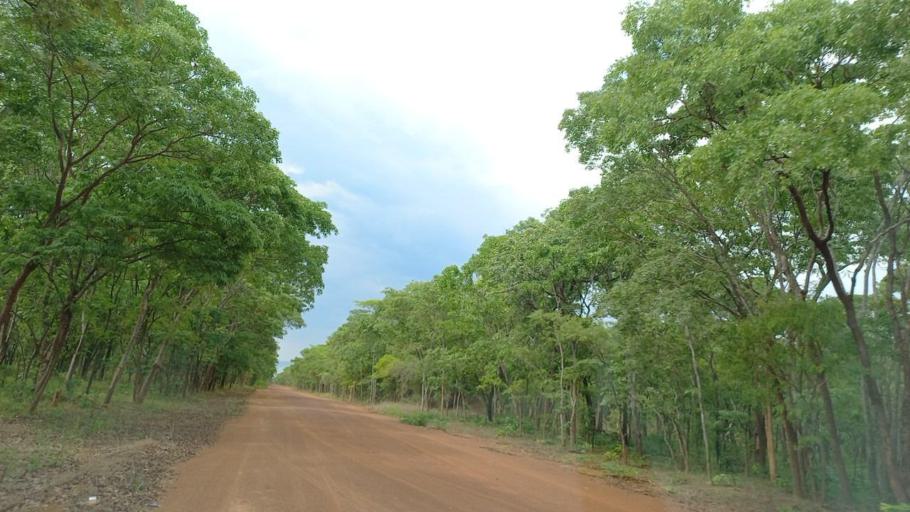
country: ZM
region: North-Western
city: Kalengwa
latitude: -13.3961
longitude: 25.0685
